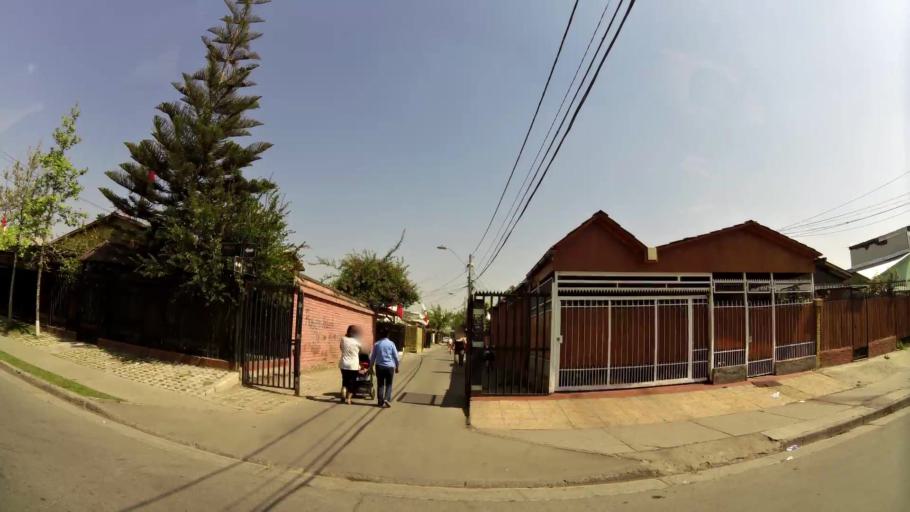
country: CL
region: Santiago Metropolitan
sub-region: Provincia de Santiago
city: La Pintana
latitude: -33.5566
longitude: -70.6102
